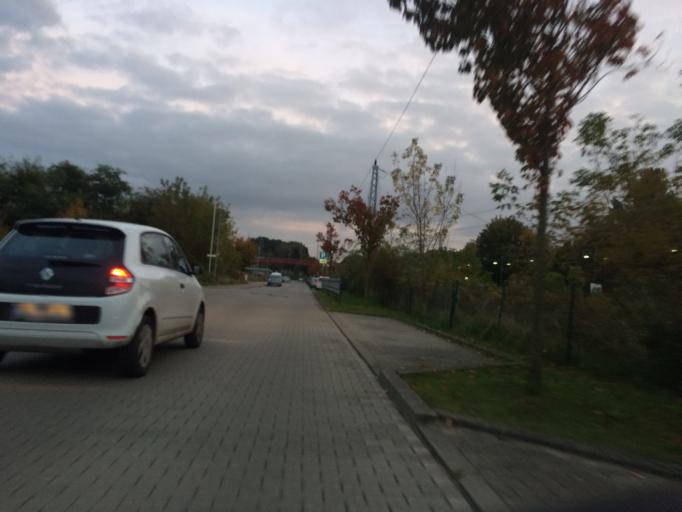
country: DE
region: Brandenburg
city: Glienicke
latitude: 52.6707
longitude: 13.3196
